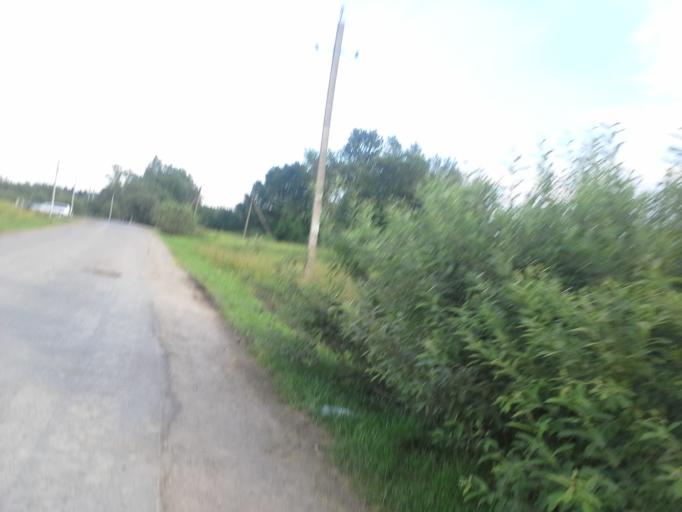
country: RU
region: Moskovskaya
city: Kievskij
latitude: 55.4640
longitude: 36.8838
